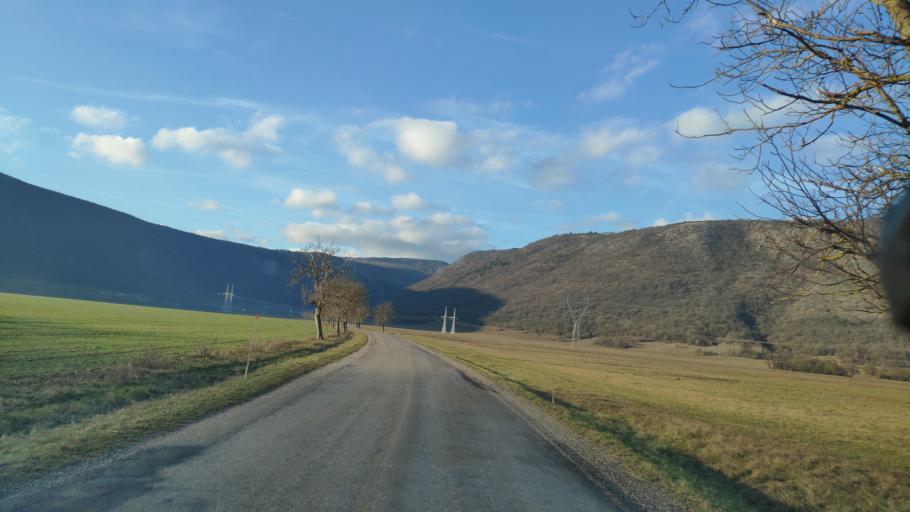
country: SK
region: Kosicky
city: Medzev
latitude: 48.6172
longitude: 20.8777
